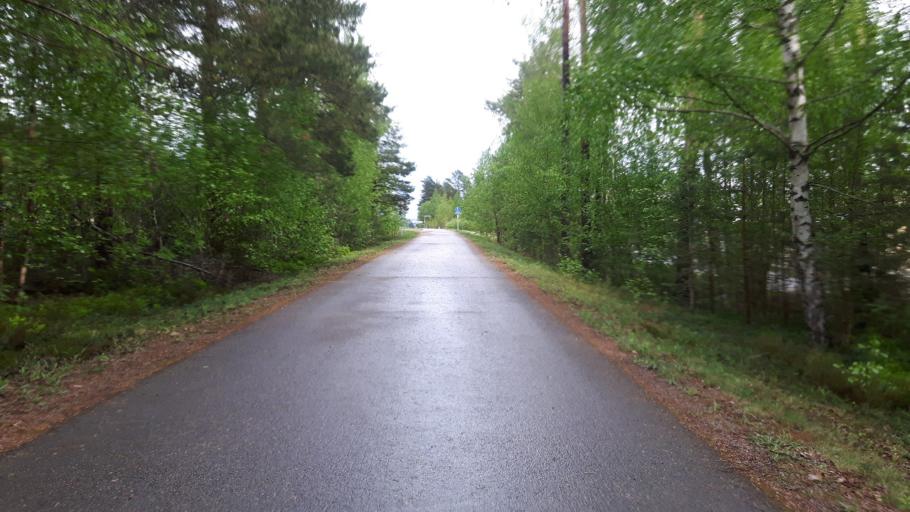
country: FI
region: Kymenlaakso
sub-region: Kotka-Hamina
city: Hamina
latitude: 60.5650
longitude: 27.1183
